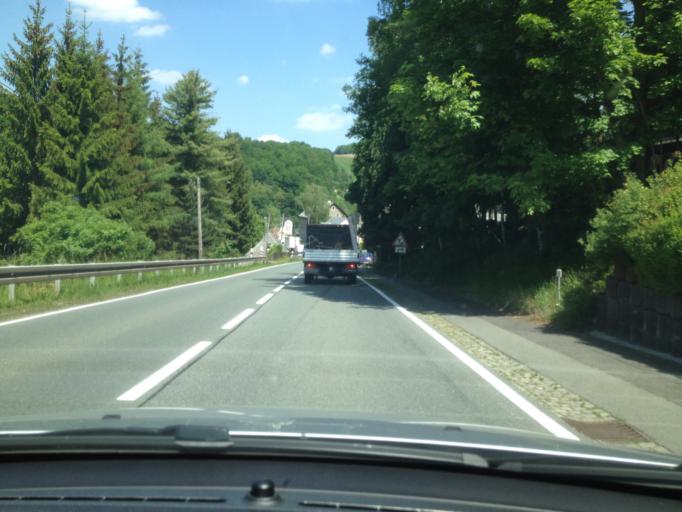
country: DE
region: Saxony
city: Burkhardtsdorf
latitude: 50.7307
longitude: 12.9305
